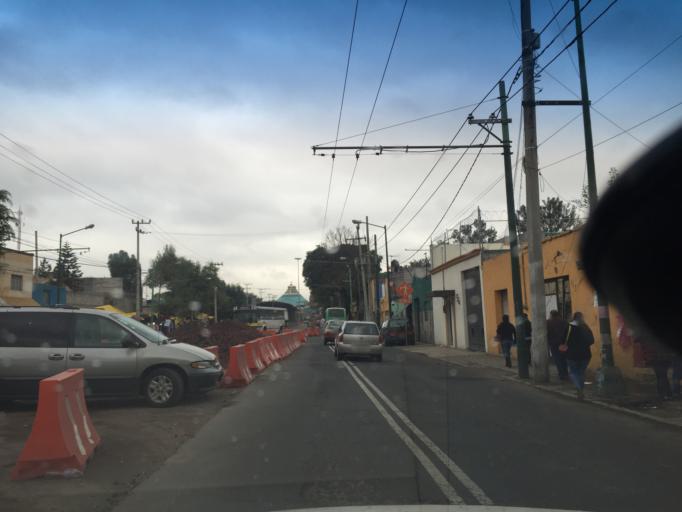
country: MX
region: Mexico City
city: Gustavo A. Madero
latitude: 19.4836
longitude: -99.1109
